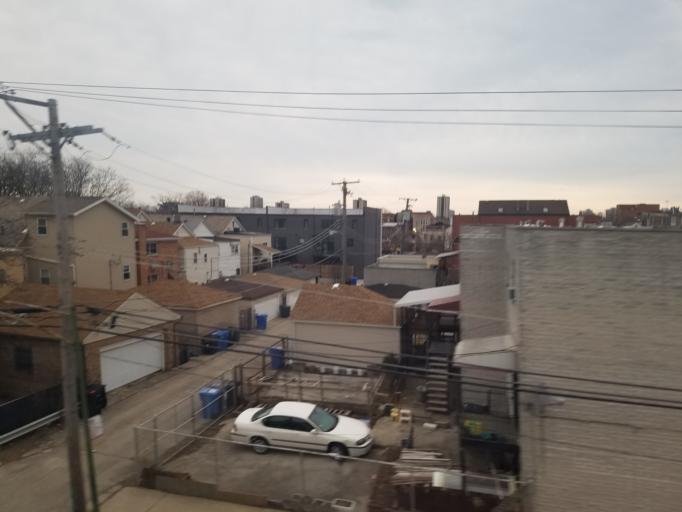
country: US
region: Illinois
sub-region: Cook County
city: Chicago
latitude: 41.8383
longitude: -87.6362
